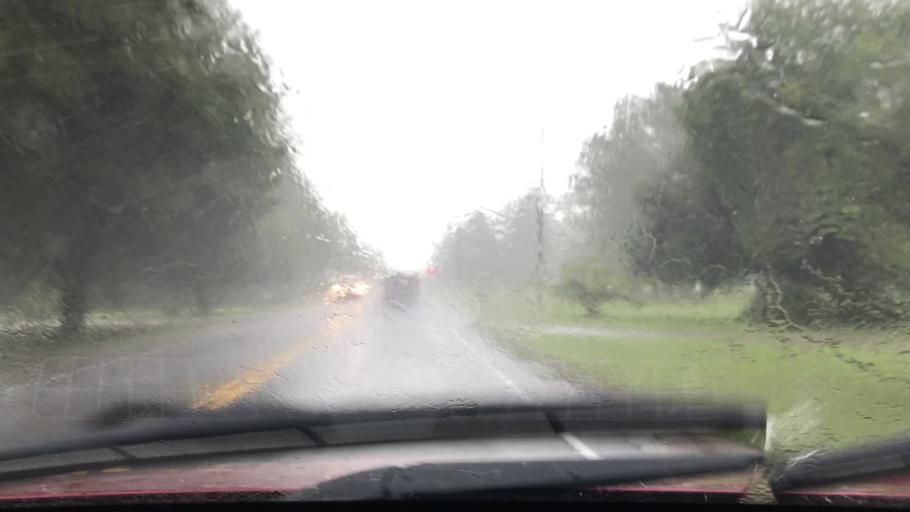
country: US
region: South Carolina
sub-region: Horry County
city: Loris
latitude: 33.9011
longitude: -78.8743
